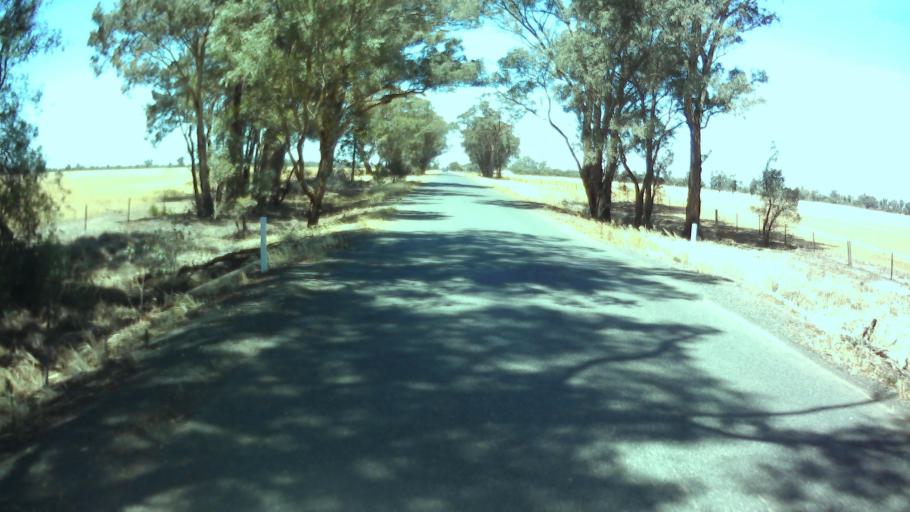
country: AU
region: New South Wales
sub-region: Weddin
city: Grenfell
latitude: -34.0232
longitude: 147.7922
